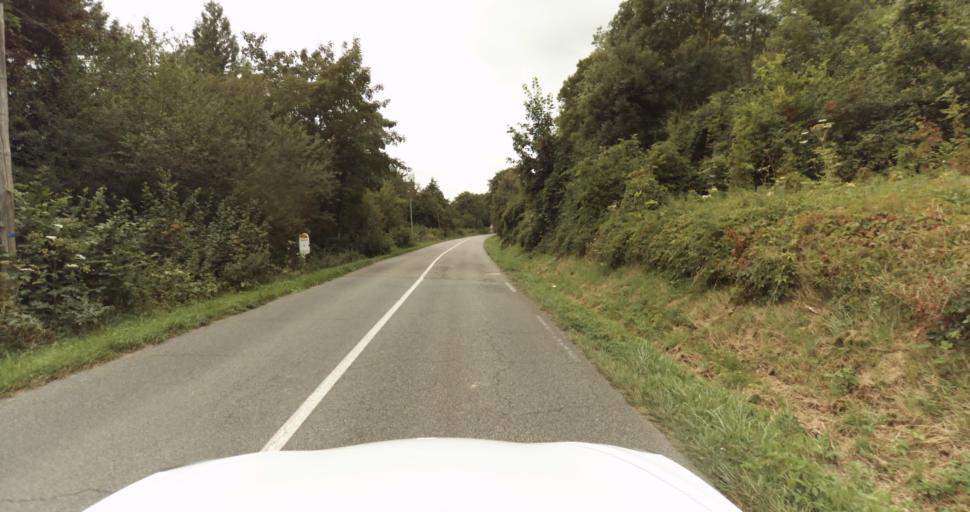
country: FR
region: Haute-Normandie
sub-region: Departement de l'Eure
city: Saint-Sebastien-de-Morsent
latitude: 48.9983
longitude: 1.0664
